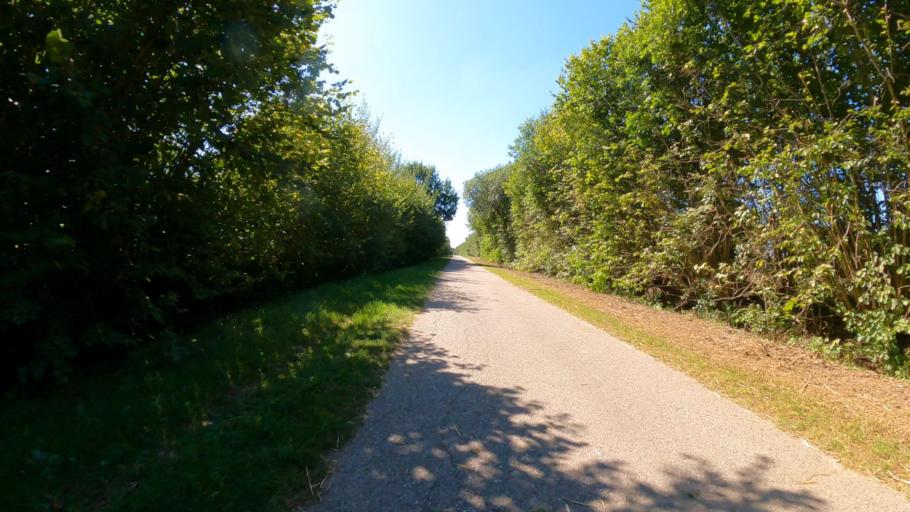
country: DE
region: Schleswig-Holstein
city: Hohenhorn
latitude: 53.4732
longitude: 10.3512
